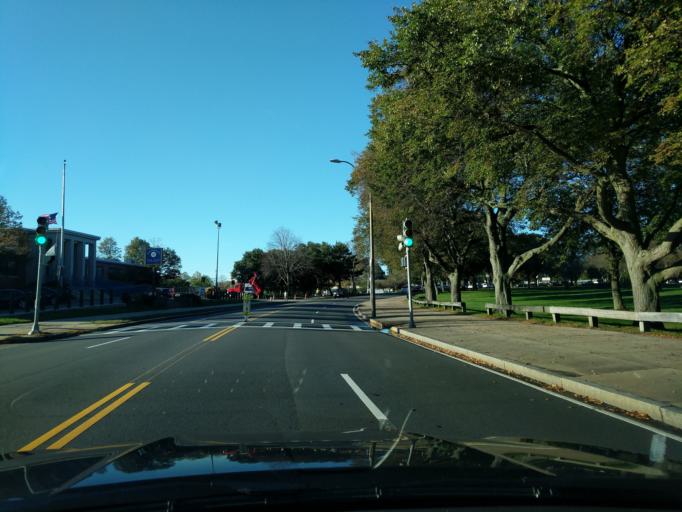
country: US
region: Massachusetts
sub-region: Suffolk County
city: South Boston
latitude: 42.3231
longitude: -71.0491
